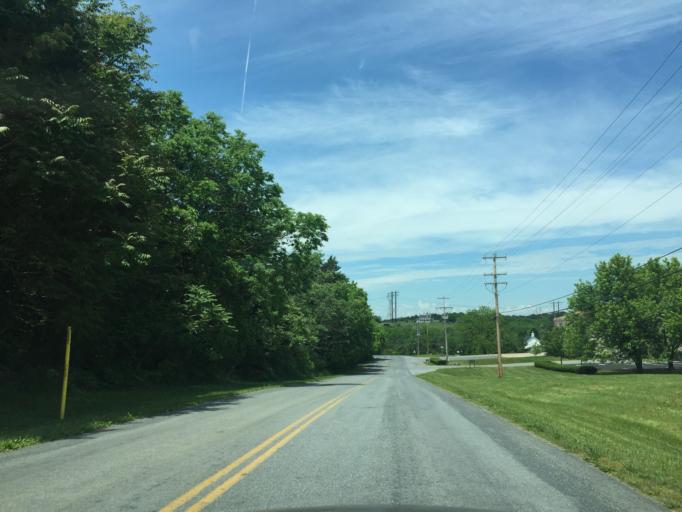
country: US
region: Virginia
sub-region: Warren County
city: Front Royal
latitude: 38.9784
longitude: -78.1812
